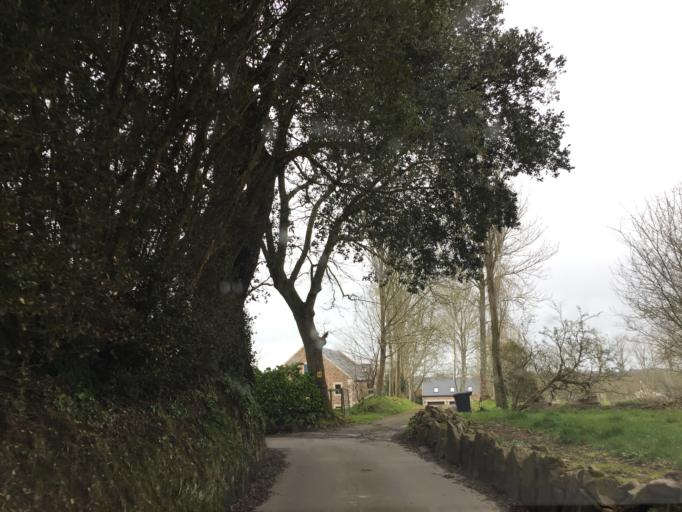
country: JE
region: St Helier
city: Saint Helier
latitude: 49.2064
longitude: -2.1480
